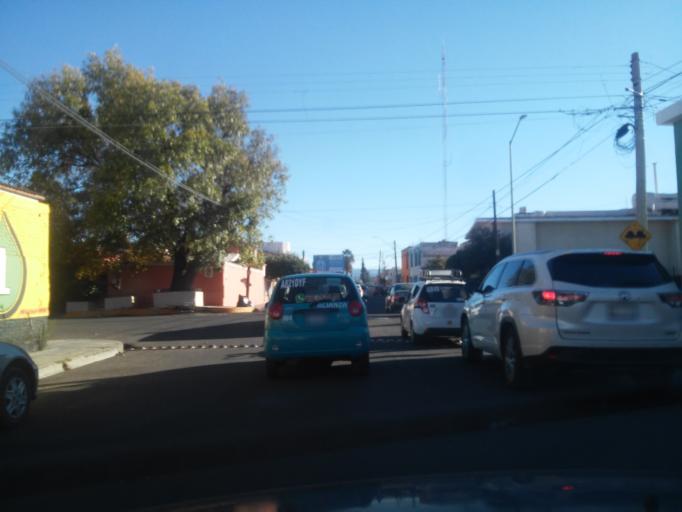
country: MX
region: Durango
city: Victoria de Durango
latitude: 24.0282
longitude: -104.6471
